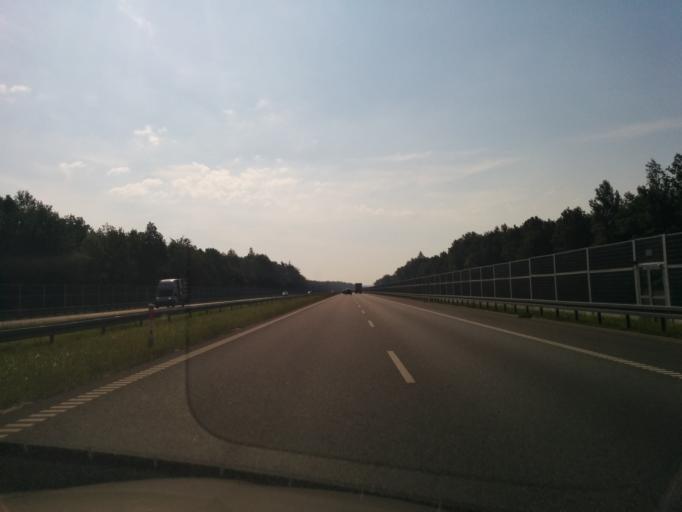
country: PL
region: Silesian Voivodeship
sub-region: Powiat tarnogorski
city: Radzionkow
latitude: 50.3854
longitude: 18.8528
